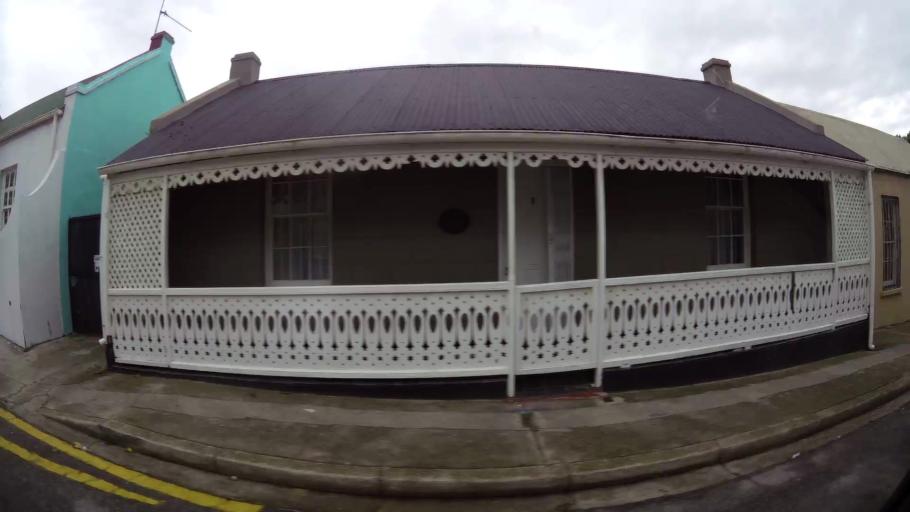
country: ZA
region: Eastern Cape
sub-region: Nelson Mandela Bay Metropolitan Municipality
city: Port Elizabeth
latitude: -33.9606
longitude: 25.6179
